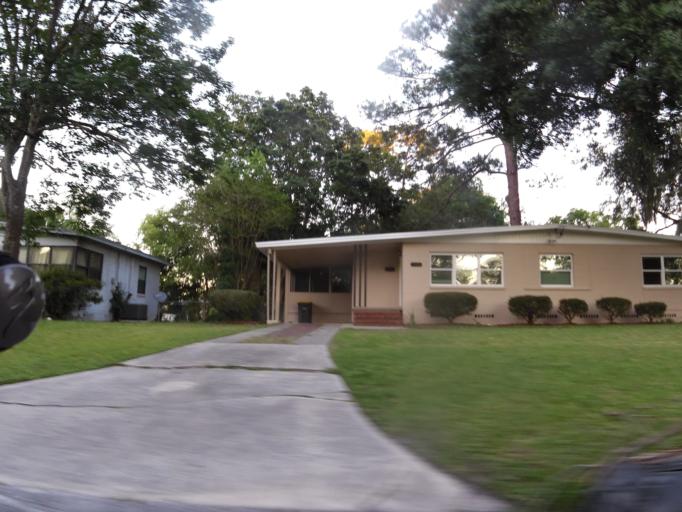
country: US
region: Florida
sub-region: Duval County
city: Jacksonville
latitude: 30.2641
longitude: -81.6360
